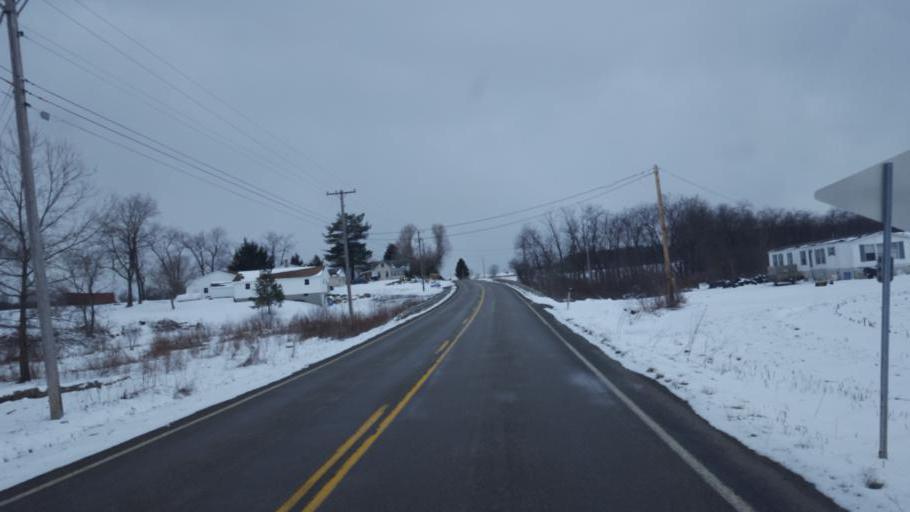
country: US
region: Pennsylvania
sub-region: Mercer County
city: Stoneboro
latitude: 41.4118
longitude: -80.0855
